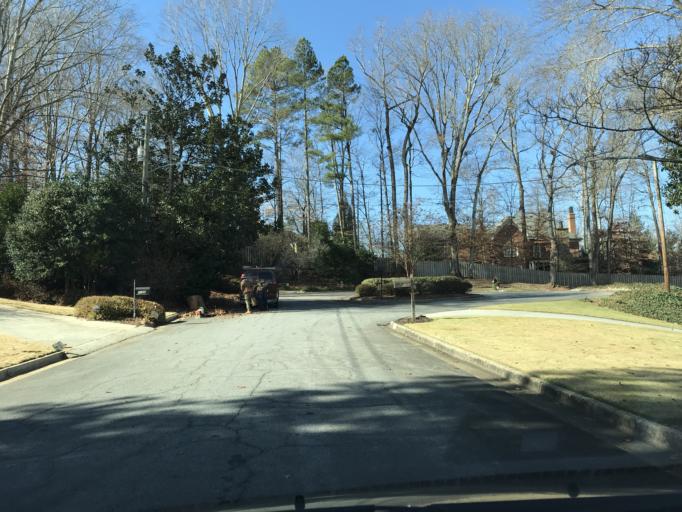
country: US
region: Georgia
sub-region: DeKalb County
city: North Atlanta
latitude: 33.8846
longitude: -84.3511
